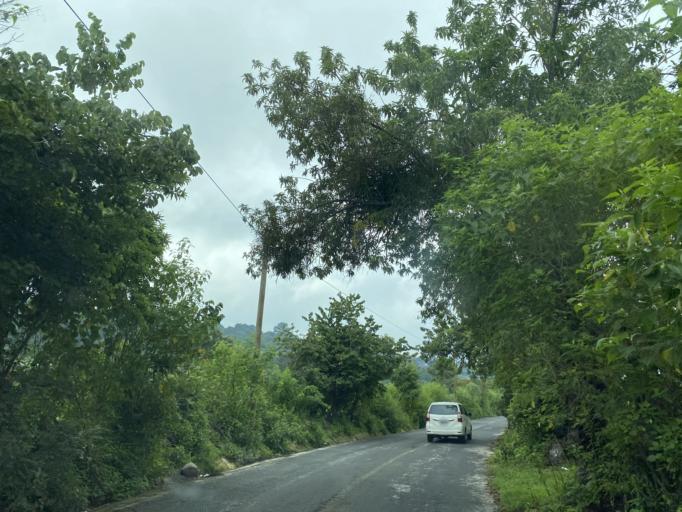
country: MX
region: Morelos
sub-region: Yecapixtla
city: Achichipico
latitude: 18.9560
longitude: -98.8259
